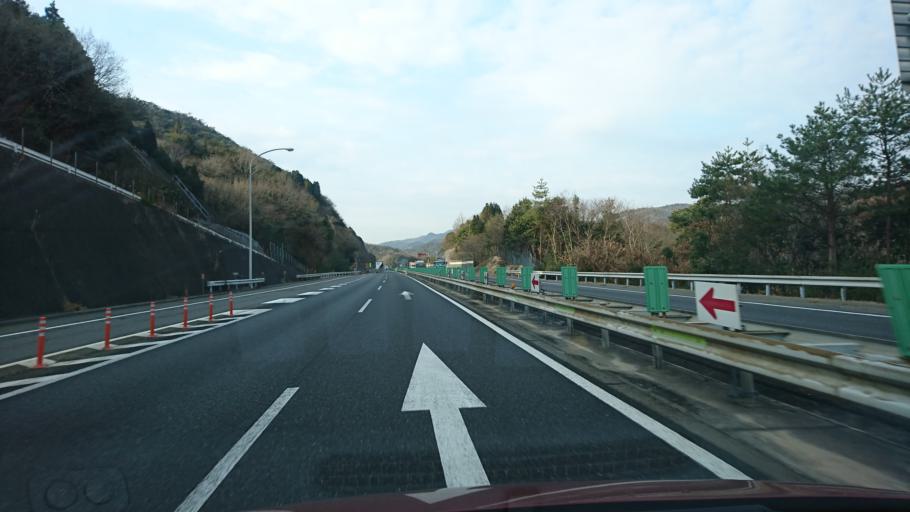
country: JP
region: Hyogo
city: Kariya
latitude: 34.7820
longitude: 134.2582
